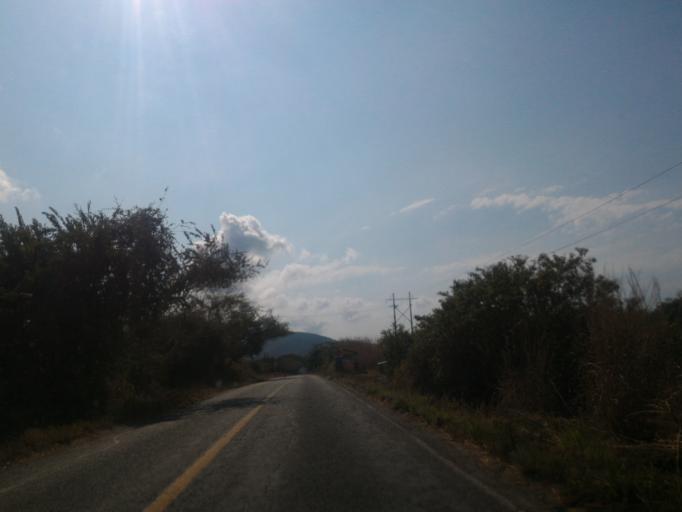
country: MX
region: Michoacan
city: Coahuayana Viejo
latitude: 18.5235
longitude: -103.5858
